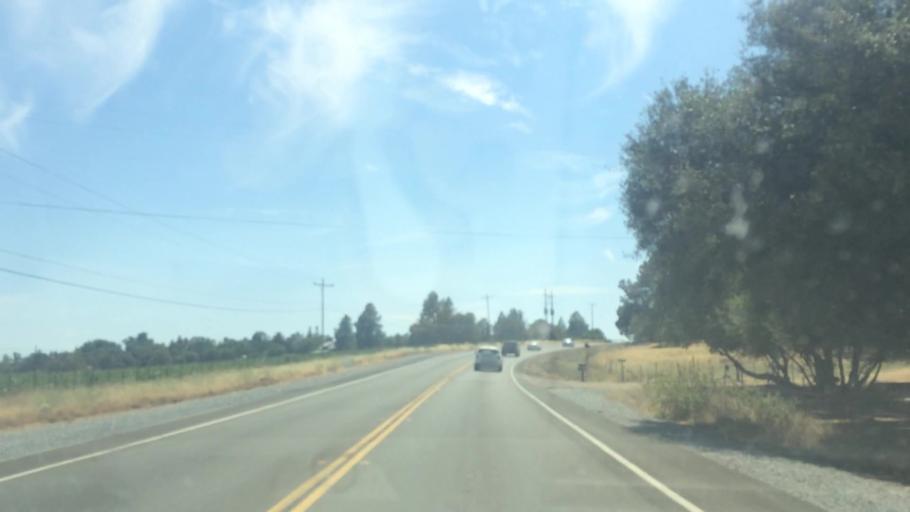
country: US
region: California
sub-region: Amador County
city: Sutter Creek
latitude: 38.3899
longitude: -120.7711
